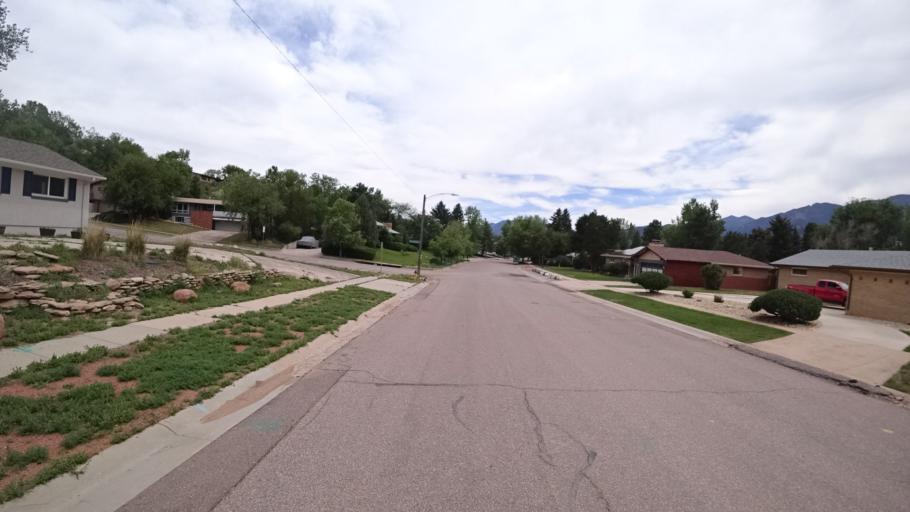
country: US
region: Colorado
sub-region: El Paso County
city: Colorado Springs
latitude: 38.8591
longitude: -104.8634
